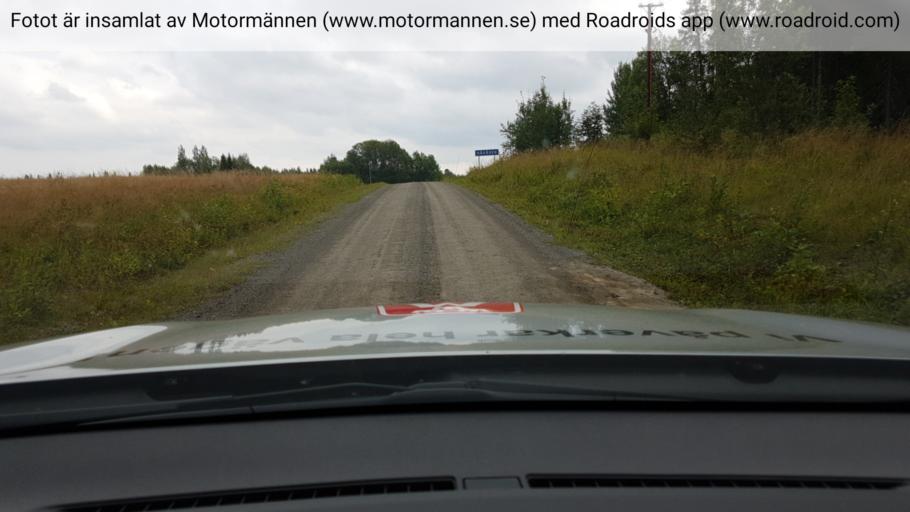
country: SE
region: Jaemtland
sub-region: Stroemsunds Kommun
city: Stroemsund
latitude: 63.7774
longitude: 15.3163
